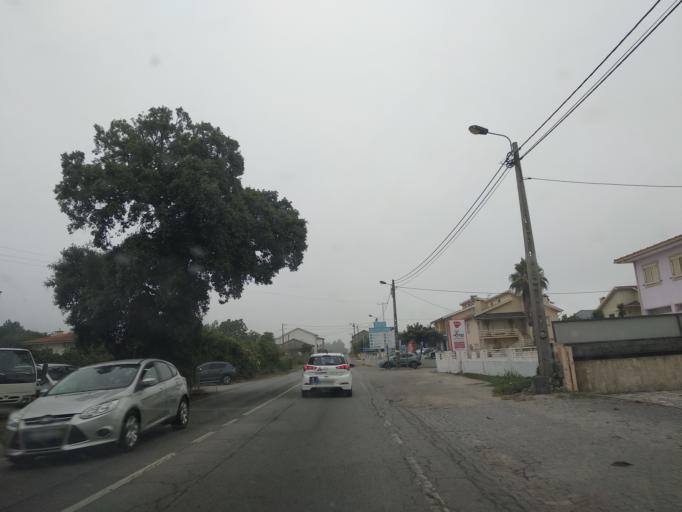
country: PT
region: Braga
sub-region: Vila Verde
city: Vila Verde
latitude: 41.6293
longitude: -8.4334
